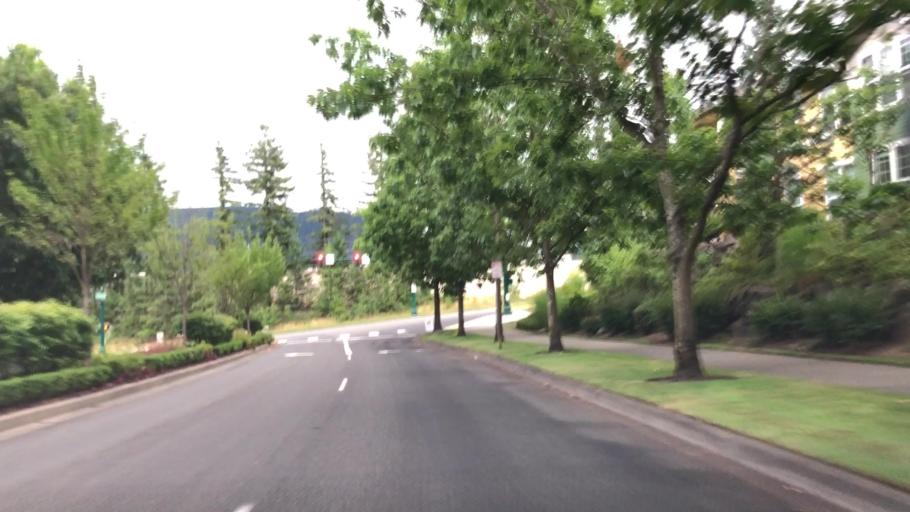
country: US
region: Washington
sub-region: King County
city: Fall City
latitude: 47.5308
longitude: -121.8684
